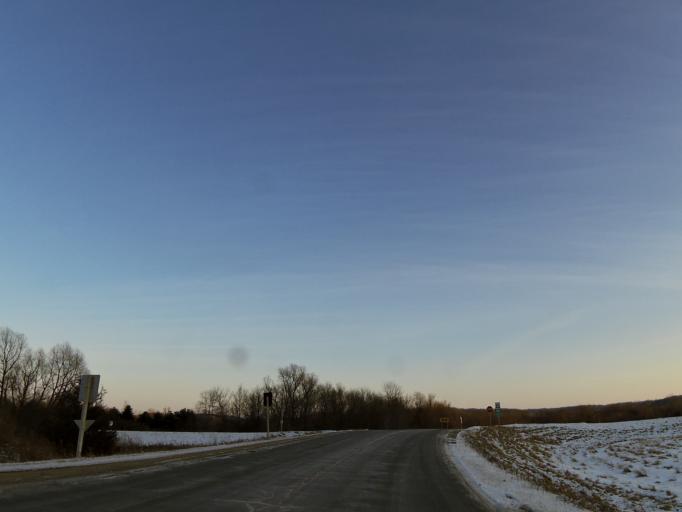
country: US
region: Wisconsin
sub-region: Pierce County
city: River Falls
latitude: 44.8979
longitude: -92.6042
